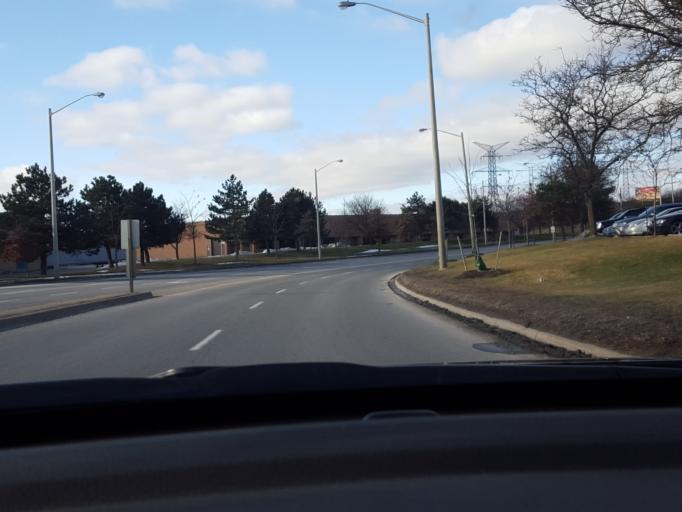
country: CA
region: Ontario
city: Concord
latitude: 43.7679
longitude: -79.5676
